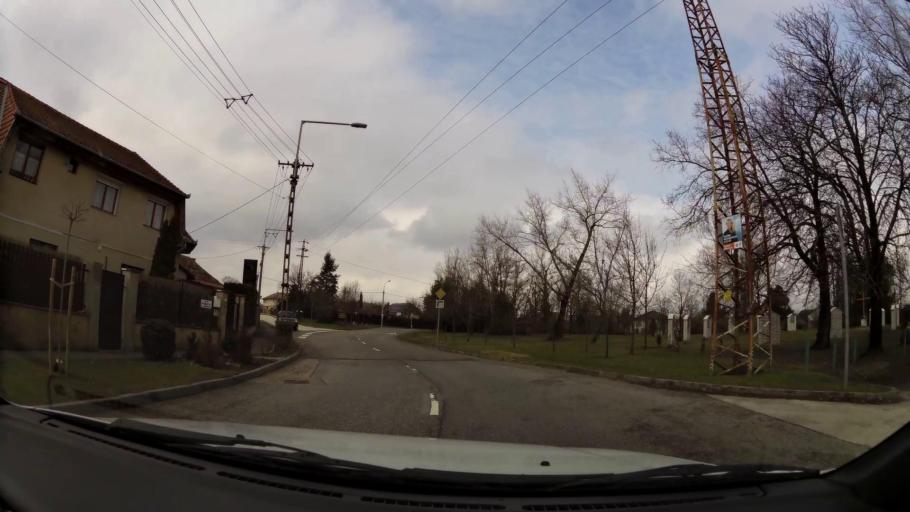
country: HU
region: Budapest
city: Budapest XVII. keruelet
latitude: 47.4948
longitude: 19.2609
